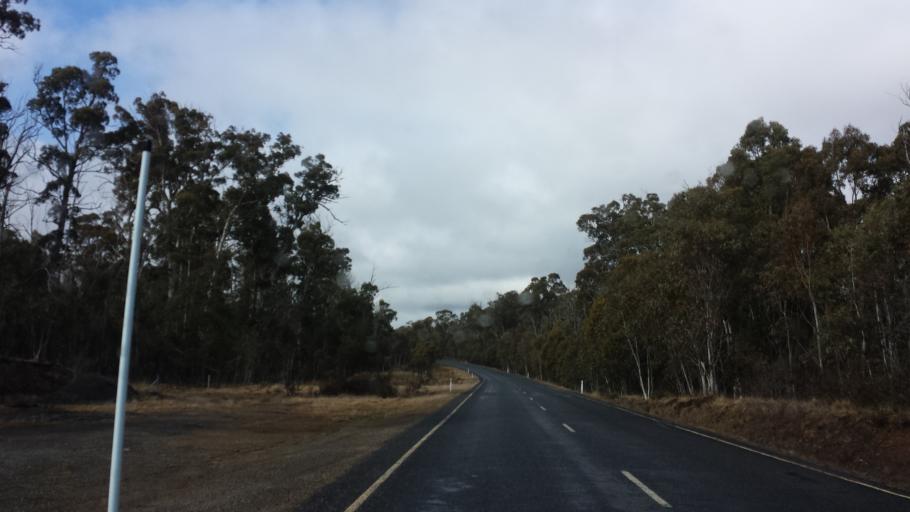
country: AU
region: Victoria
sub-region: Alpine
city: Mount Beauty
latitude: -37.0668
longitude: 147.3415
